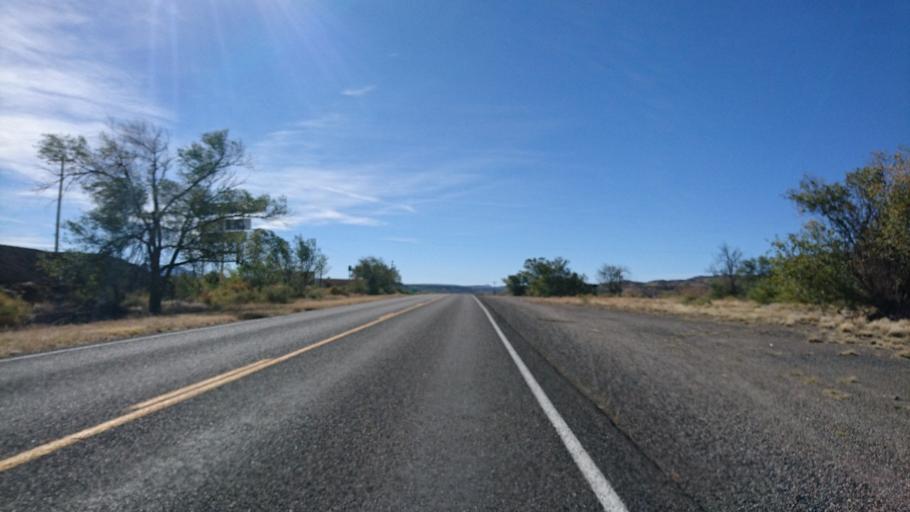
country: US
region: New Mexico
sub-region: Cibola County
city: Skyline-Ganipa
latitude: 35.0774
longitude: -107.6458
